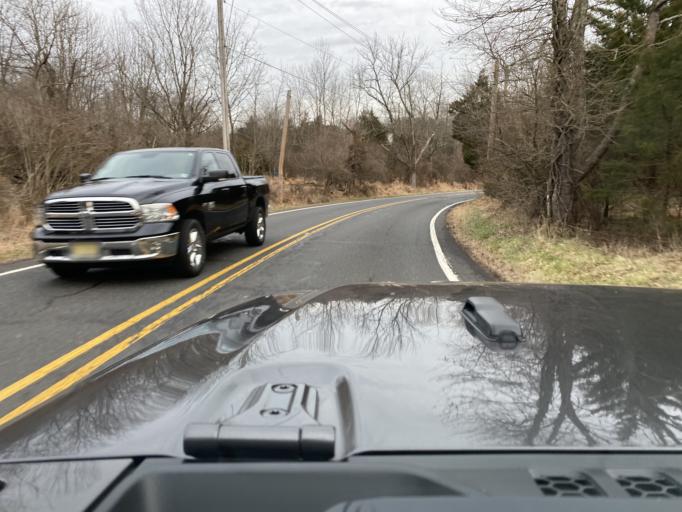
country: US
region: New Jersey
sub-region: Hunterdon County
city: Whitehouse Station
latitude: 40.5303
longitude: -74.7408
